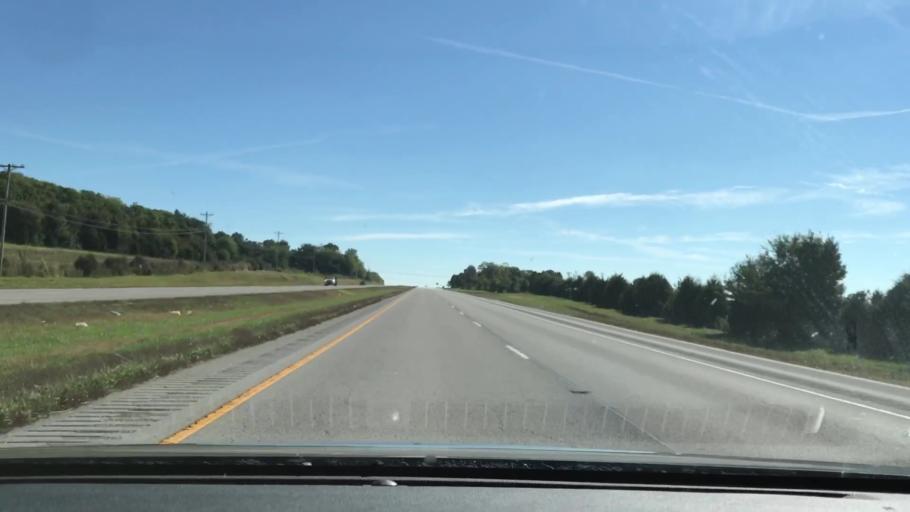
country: US
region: Kentucky
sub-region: Todd County
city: Elkton
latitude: 36.8248
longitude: -87.2105
